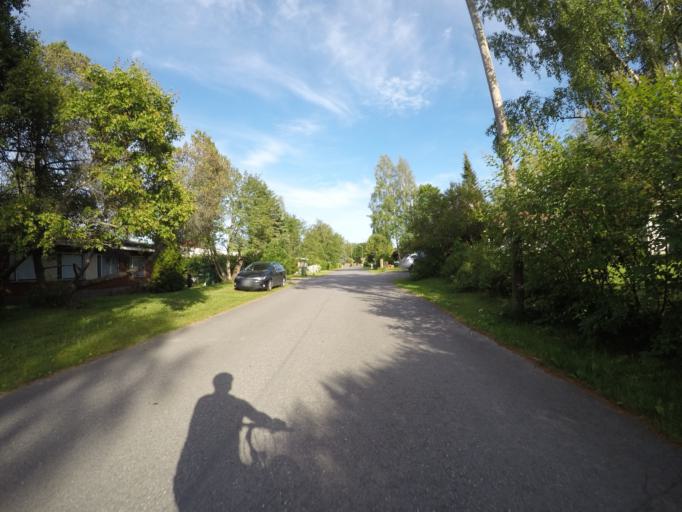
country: FI
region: Haeme
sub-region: Haemeenlinna
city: Haemeenlinna
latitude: 60.9788
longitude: 24.4180
